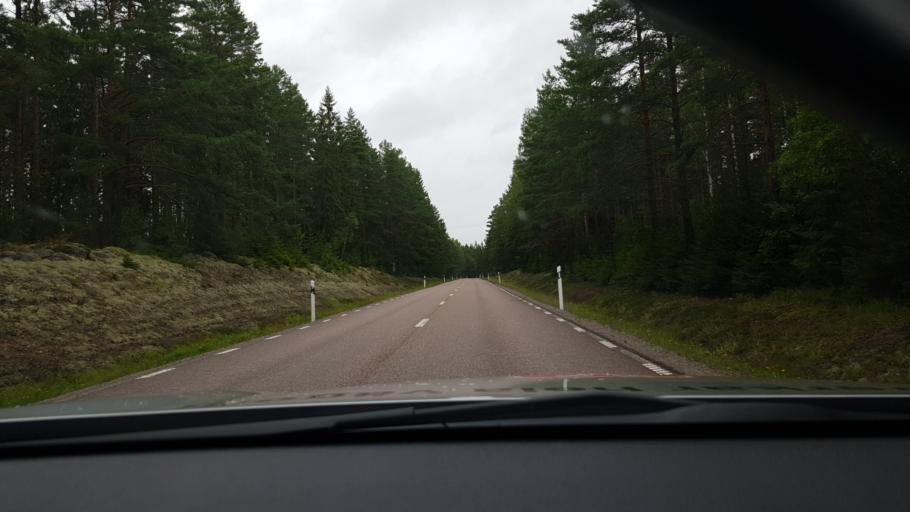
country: SE
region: Gaevleborg
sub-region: Gavle Kommun
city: Hedesunda
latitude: 60.3239
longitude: 16.9177
